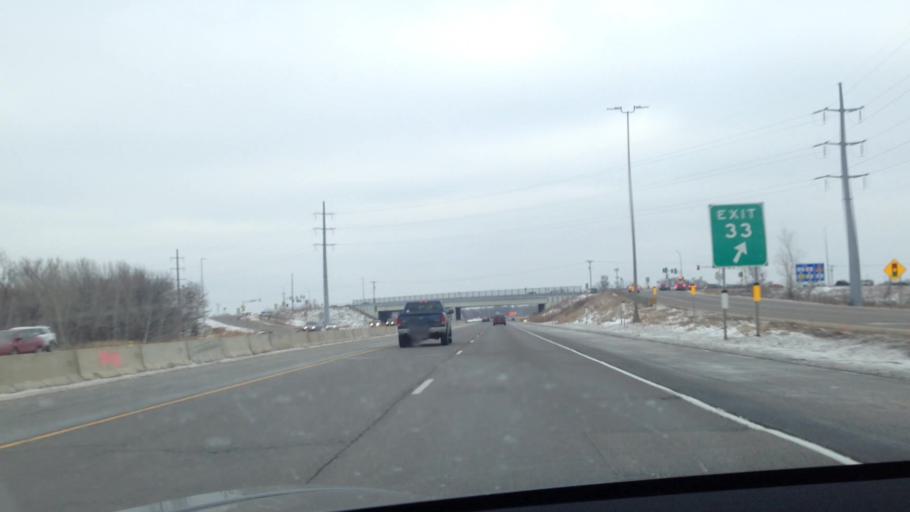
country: US
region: Minnesota
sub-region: Anoka County
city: Lexington
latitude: 45.1571
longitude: -93.1663
